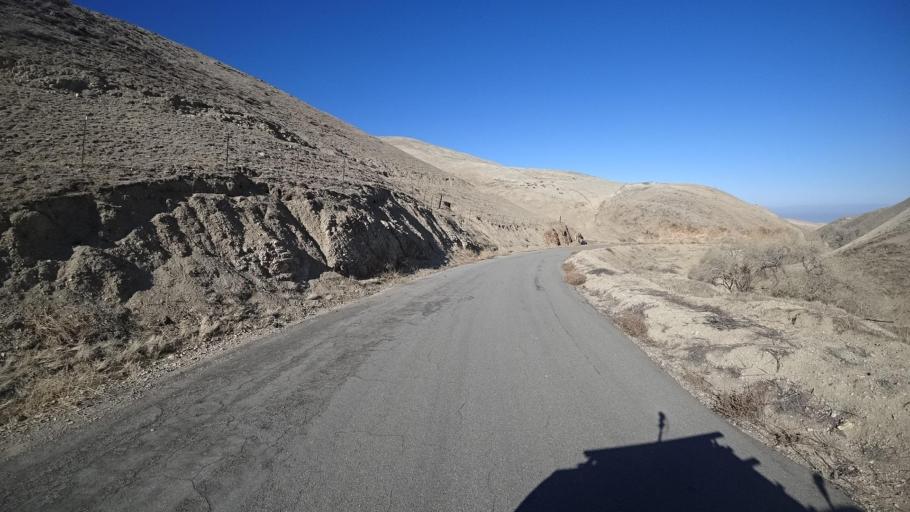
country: US
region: California
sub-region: Kern County
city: Maricopa
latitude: 34.9691
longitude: -119.4143
